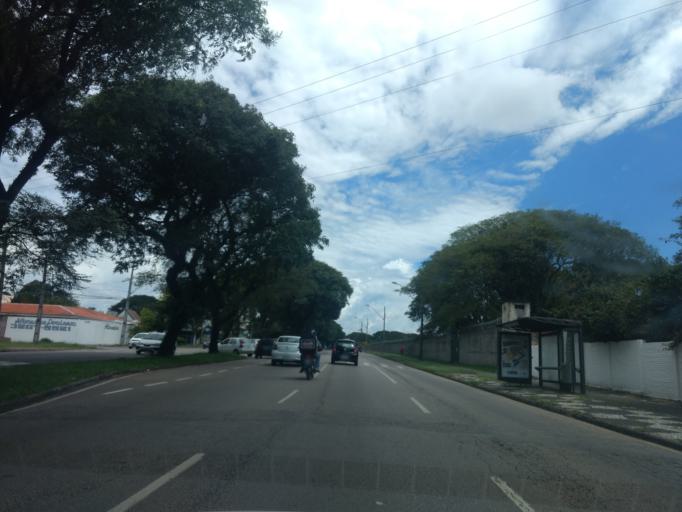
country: BR
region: Parana
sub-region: Pinhais
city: Pinhais
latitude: -25.4290
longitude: -49.2232
